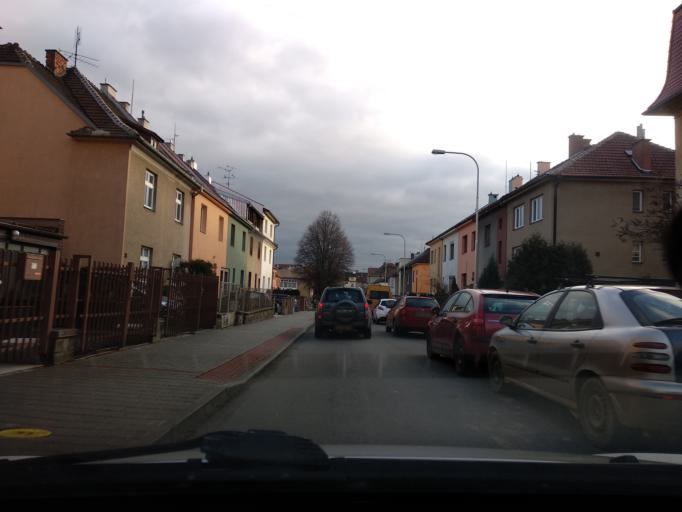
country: CZ
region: South Moravian
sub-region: Mesto Brno
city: Brno
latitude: 49.2132
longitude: 16.6197
